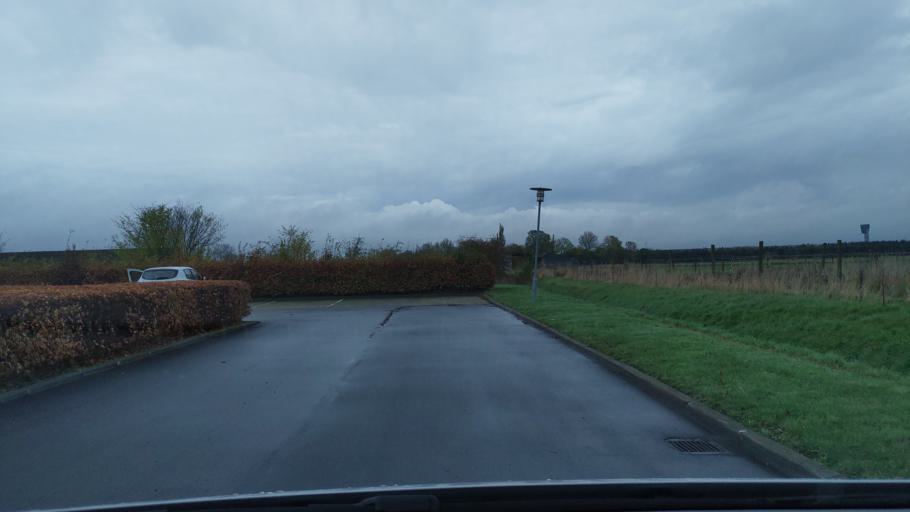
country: DK
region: Capital Region
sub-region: Dragor Kommune
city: Dragor
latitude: 55.5970
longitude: 12.6387
